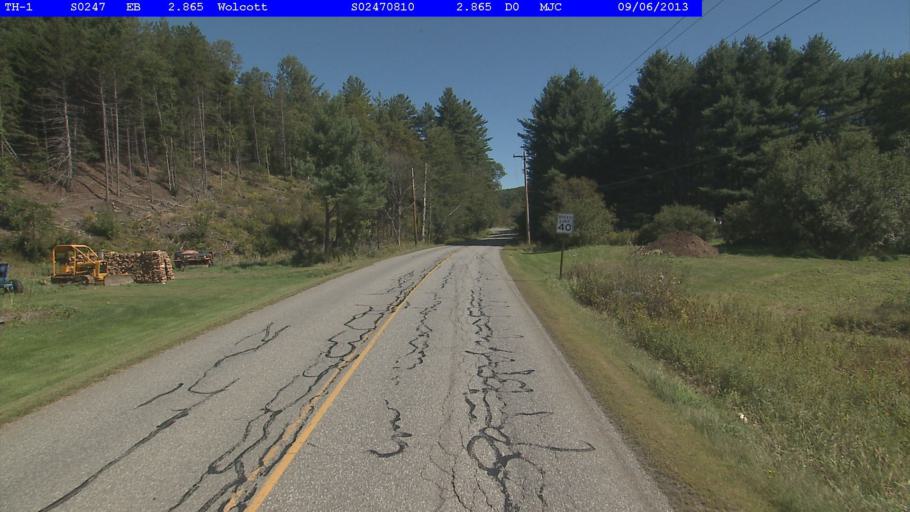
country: US
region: Vermont
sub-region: Lamoille County
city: Morrisville
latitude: 44.5958
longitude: -72.4706
